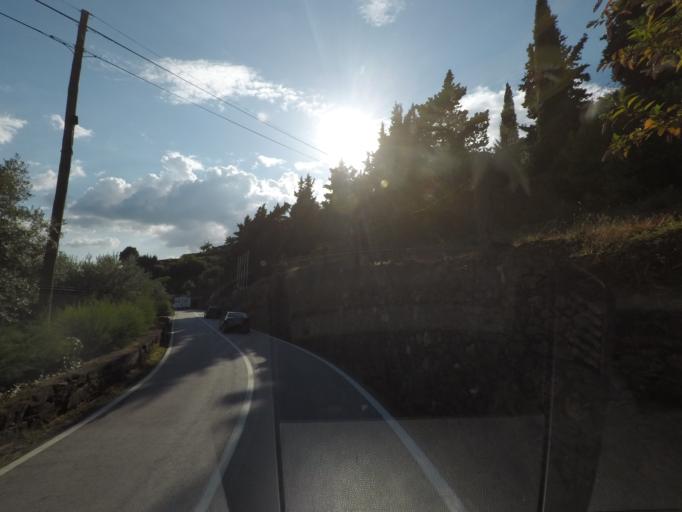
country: PT
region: Vila Real
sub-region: Mesao Frio
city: Mesao Frio
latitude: 41.1622
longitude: -7.8754
